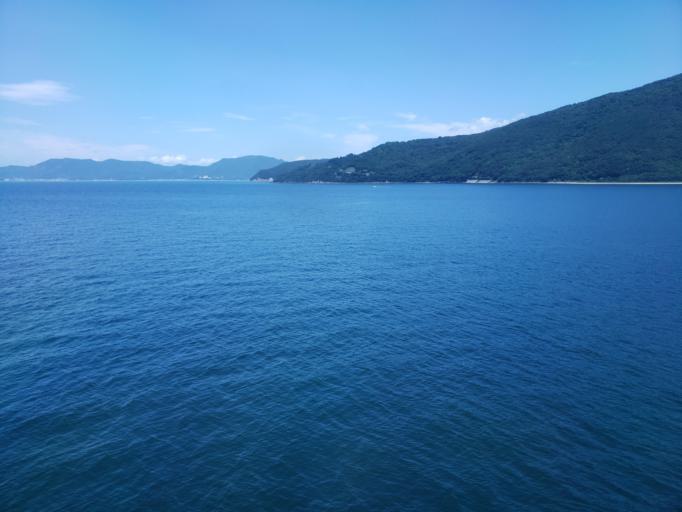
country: JP
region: Kagawa
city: Tonosho
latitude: 34.4071
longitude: 134.2239
